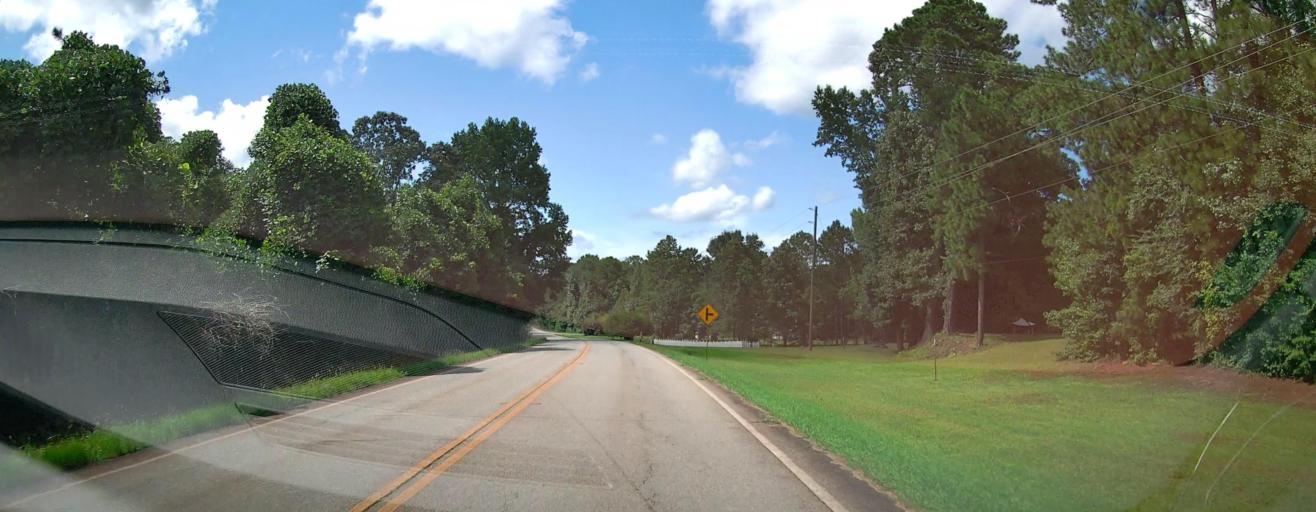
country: US
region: Georgia
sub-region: Crawford County
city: Knoxville
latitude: 32.8795
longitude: -83.9976
